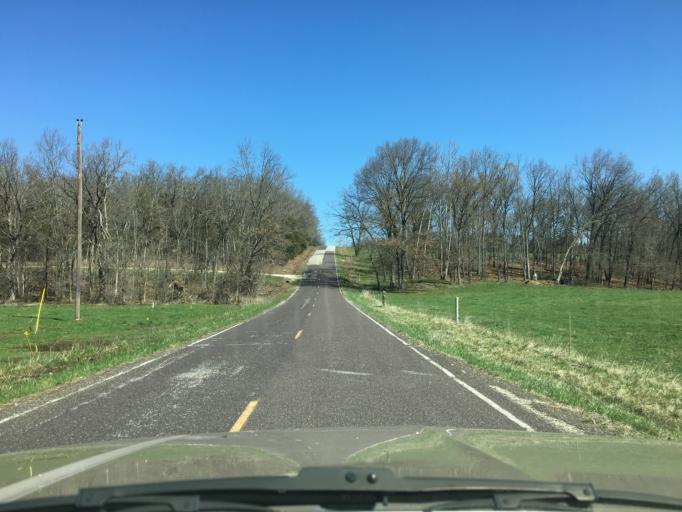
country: US
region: Missouri
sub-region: Franklin County
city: New Haven
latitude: 38.5475
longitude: -91.3302
